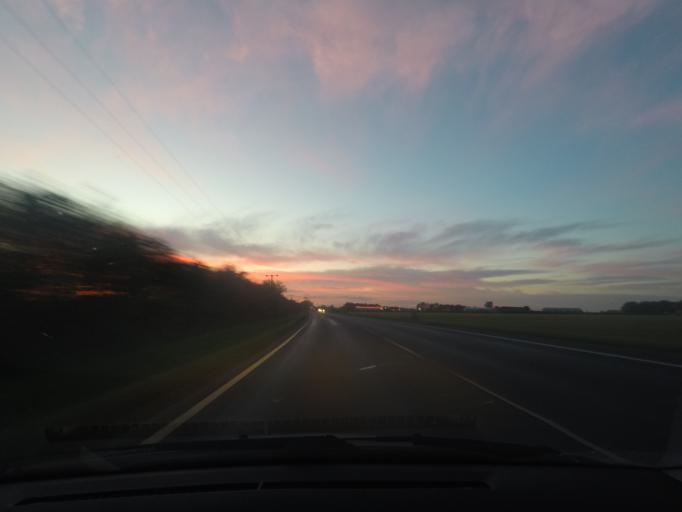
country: GB
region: England
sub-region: East Riding of Yorkshire
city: Pocklington
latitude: 53.9189
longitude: -0.7893
